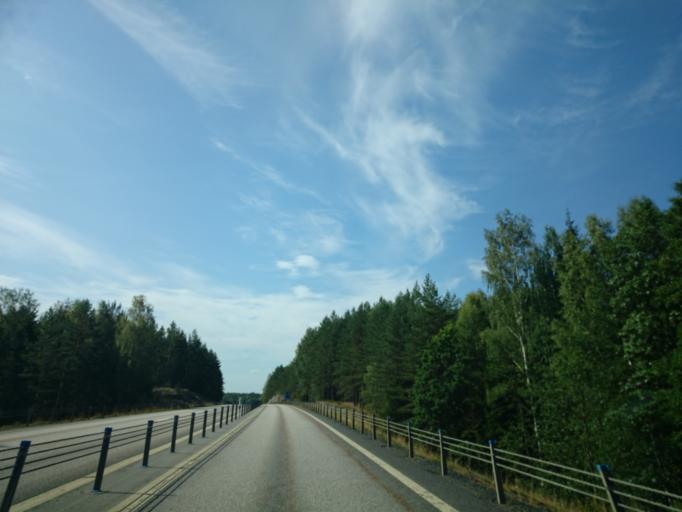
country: SE
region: OEstergoetland
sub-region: Valdemarsviks Kommun
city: Valdemarsvik
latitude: 58.1300
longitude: 16.5324
